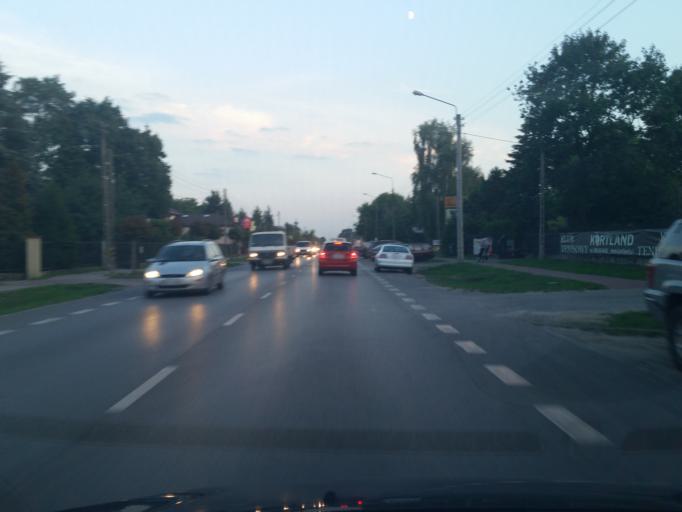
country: PL
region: Masovian Voivodeship
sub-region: Powiat legionowski
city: Jablonna
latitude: 52.3730
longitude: 20.9267
